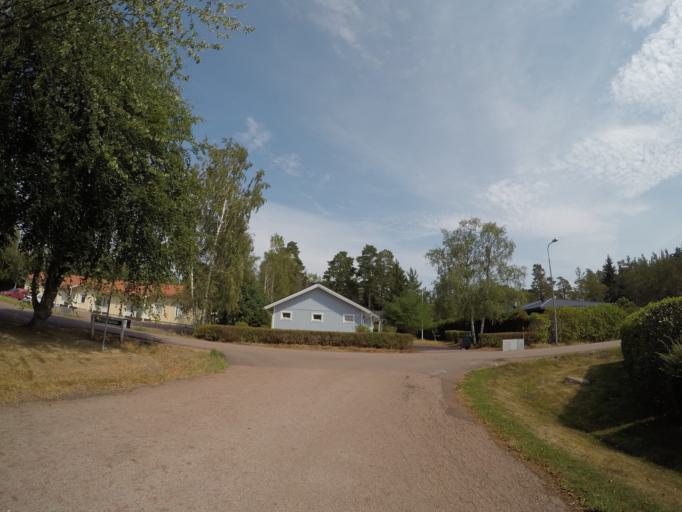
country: AX
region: Alands landsbygd
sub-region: Finstroem
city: Finstroem
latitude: 60.2357
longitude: 19.9770
